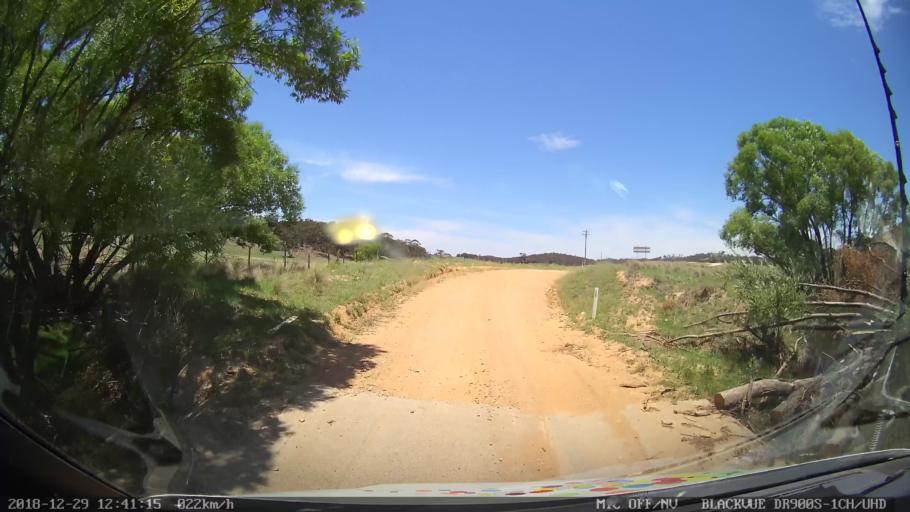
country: AU
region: Australian Capital Territory
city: Macarthur
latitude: -35.6072
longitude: 149.2228
